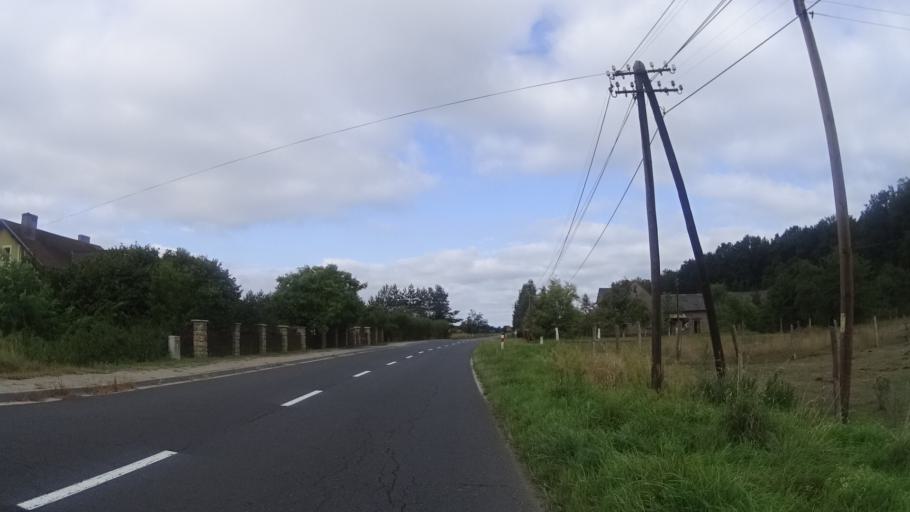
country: PL
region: Lubusz
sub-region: Powiat zarski
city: Przewoz
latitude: 51.4791
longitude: 14.9434
